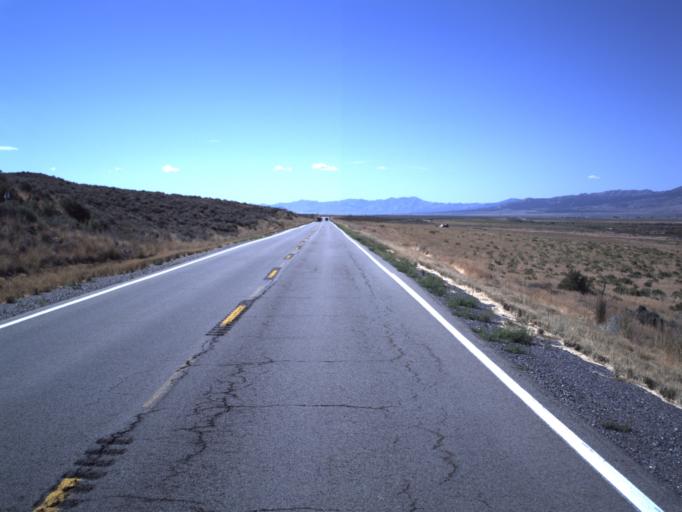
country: US
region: Utah
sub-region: Tooele County
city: Tooele
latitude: 40.4221
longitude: -112.3815
